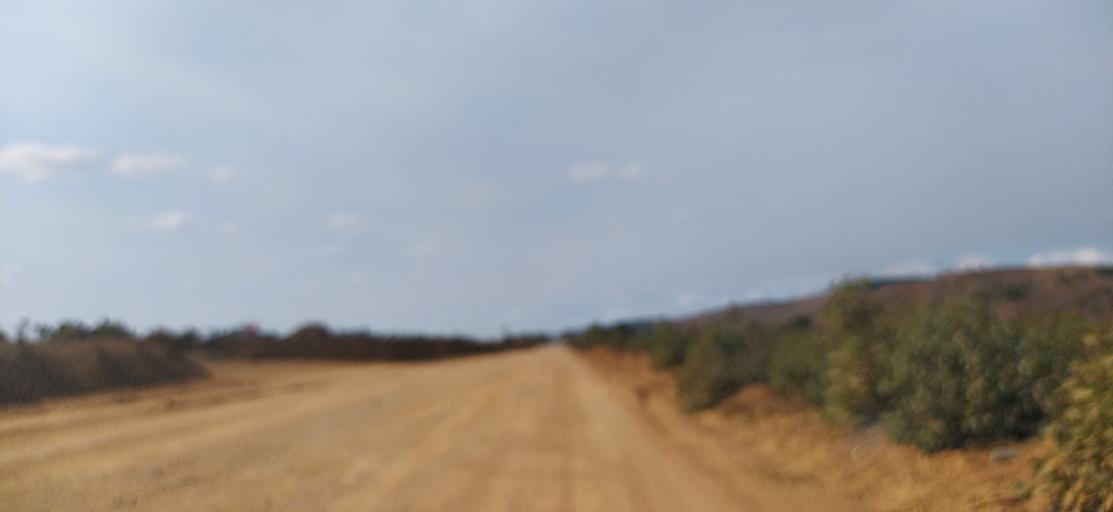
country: MG
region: Alaotra Mangoro
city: Moramanga
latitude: -18.6768
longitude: 48.2728
